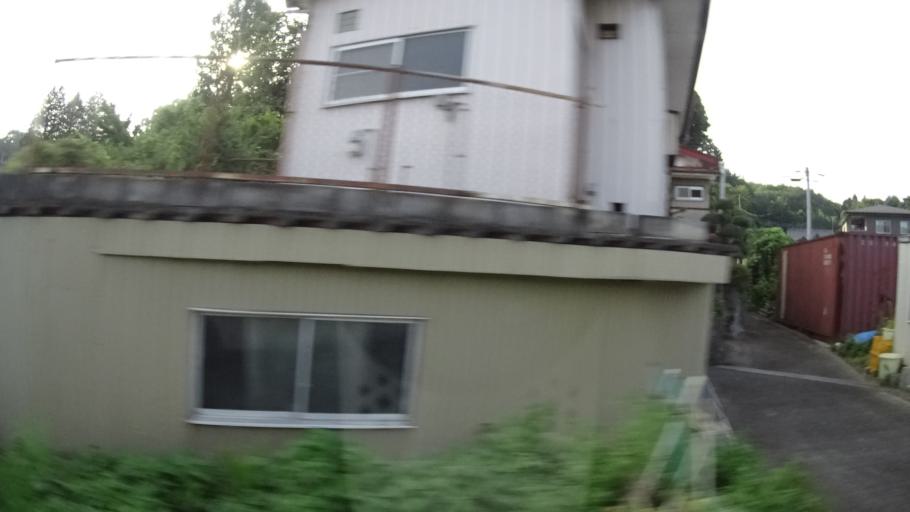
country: JP
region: Tochigi
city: Karasuyama
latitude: 36.5860
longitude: 140.1140
